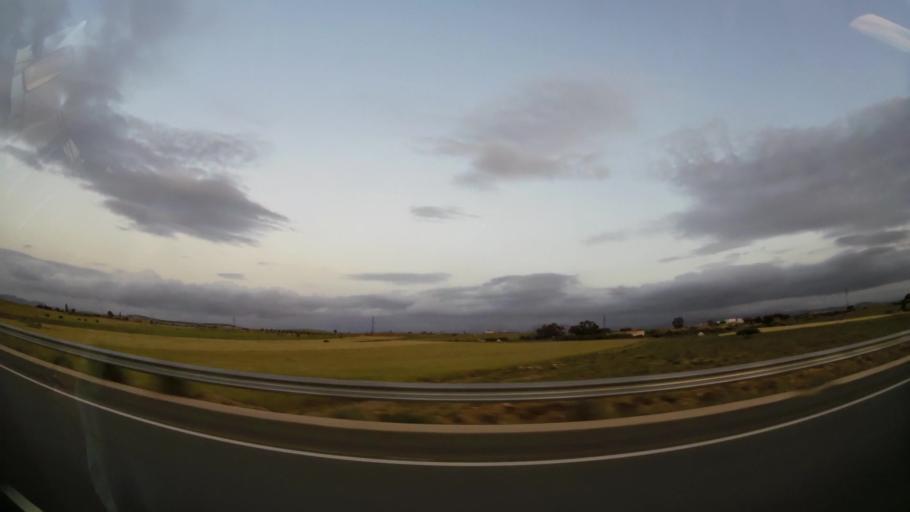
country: MA
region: Oriental
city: El Aioun
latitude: 34.6224
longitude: -2.5448
